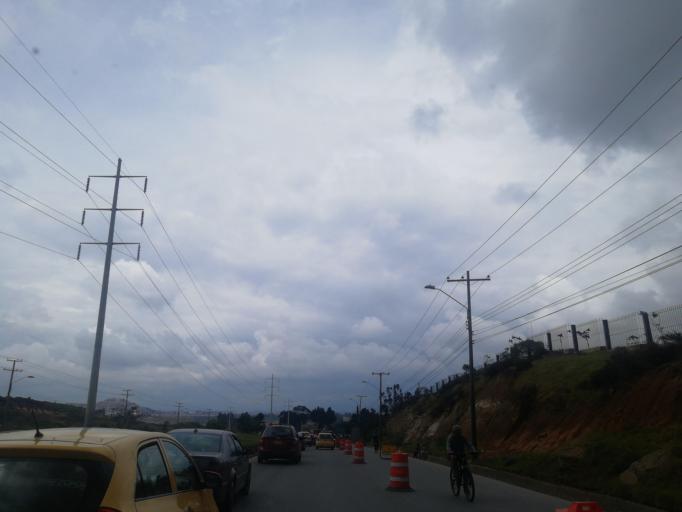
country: CO
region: Bogota D.C.
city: Bogota
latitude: 4.5306
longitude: -74.1269
